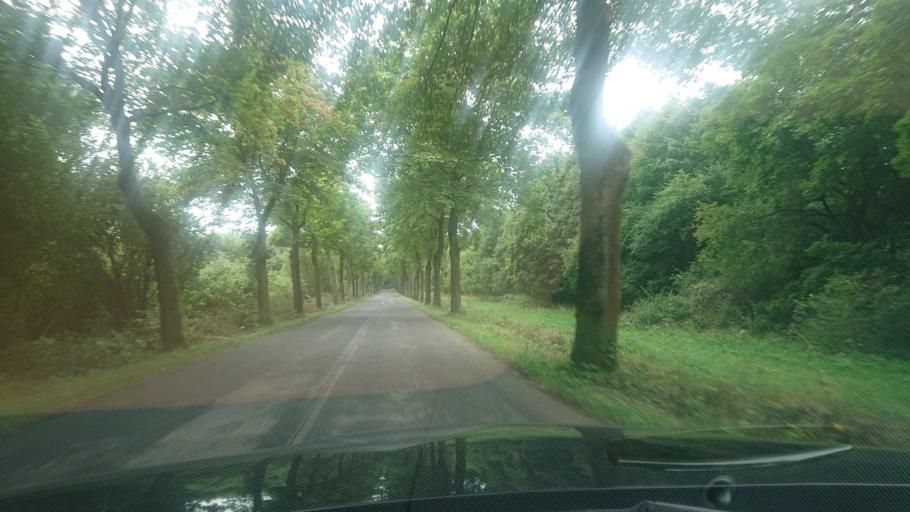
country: PL
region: Lower Silesian Voivodeship
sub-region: Powiat klodzki
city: Miedzylesie
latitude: 50.2211
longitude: 16.7123
